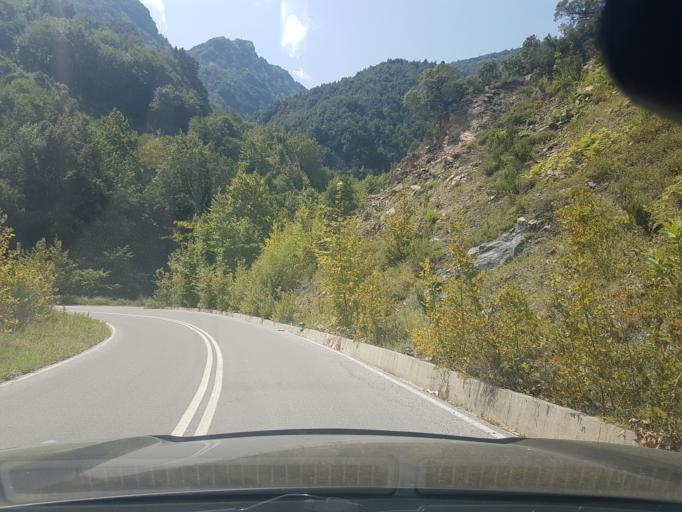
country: GR
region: Central Greece
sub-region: Nomos Evvoias
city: Kymi
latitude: 38.6296
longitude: 23.9430
